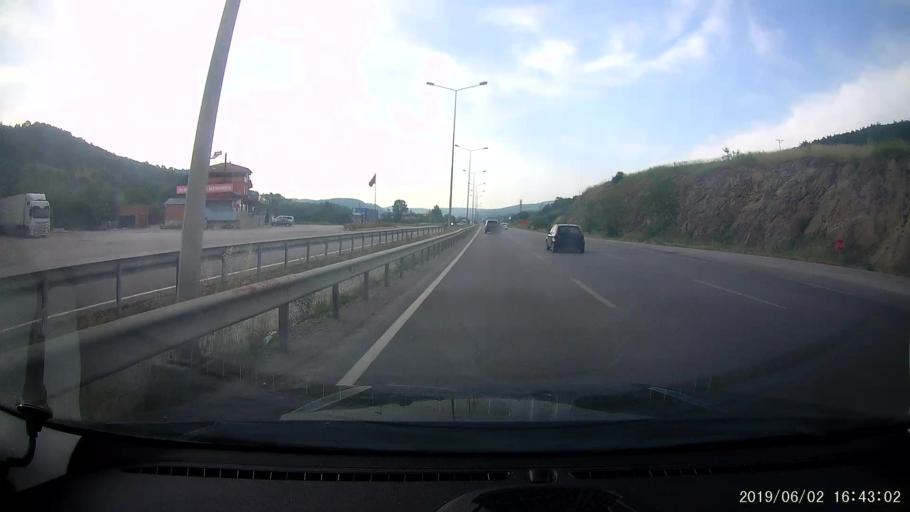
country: TR
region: Samsun
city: Kavak
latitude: 41.1288
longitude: 36.1349
